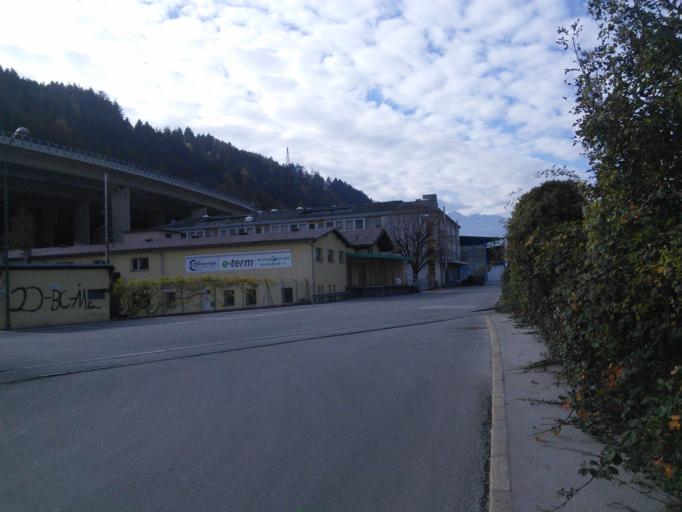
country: AT
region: Tyrol
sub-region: Innsbruck Stadt
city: Innsbruck
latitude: 47.2546
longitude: 11.3896
